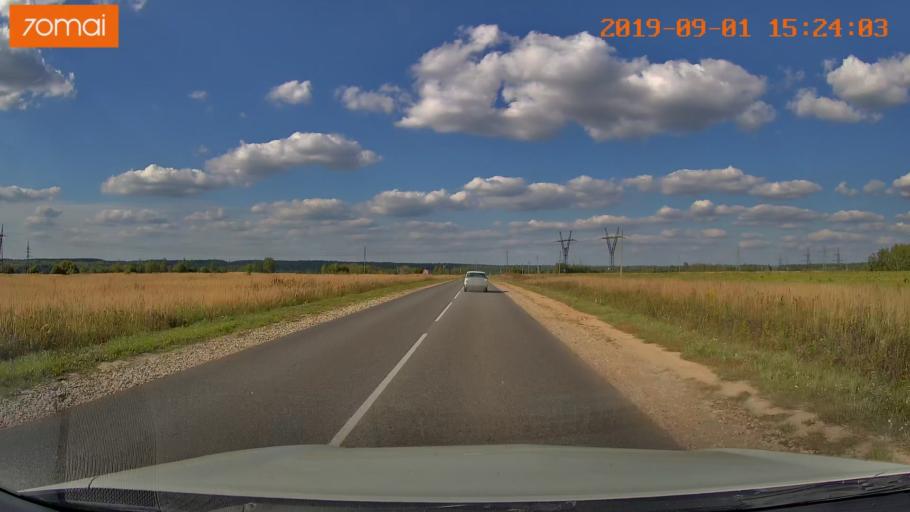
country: RU
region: Kaluga
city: Maloyaroslavets
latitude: 54.9500
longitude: 36.4585
